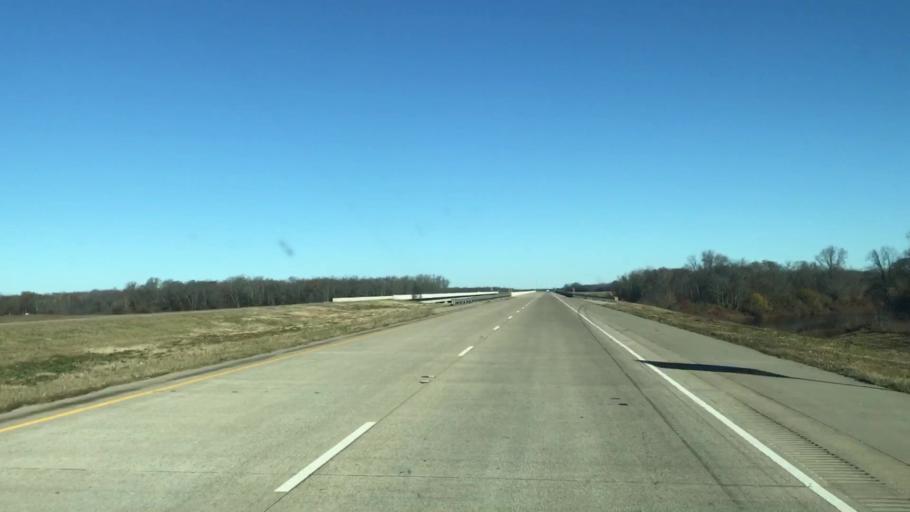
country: US
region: Louisiana
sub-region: Caddo Parish
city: Blanchard
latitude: 32.6221
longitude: -93.8358
